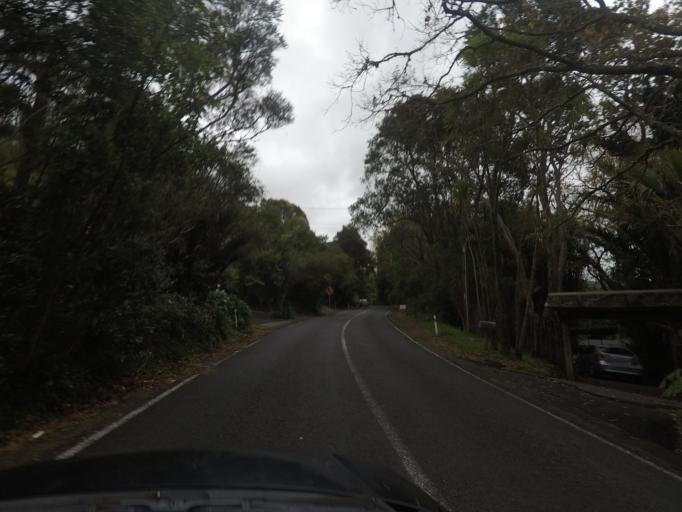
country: NZ
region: Auckland
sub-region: Auckland
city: Titirangi
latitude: -36.9242
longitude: 174.5996
